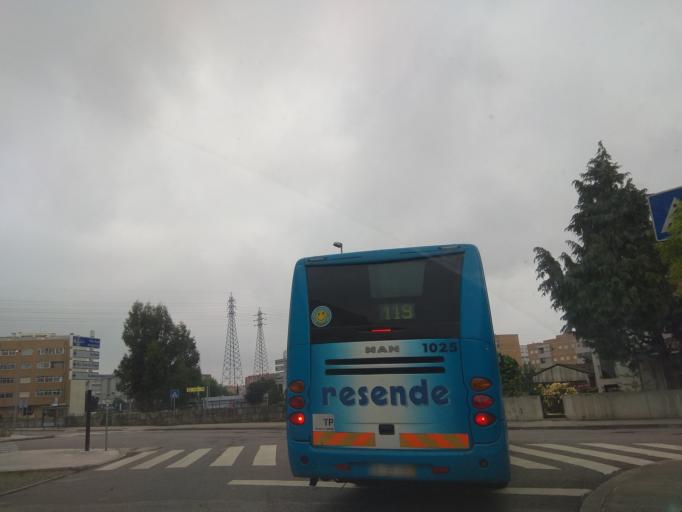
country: PT
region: Porto
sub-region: Matosinhos
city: Senhora da Hora
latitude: 41.1923
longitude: -8.6599
